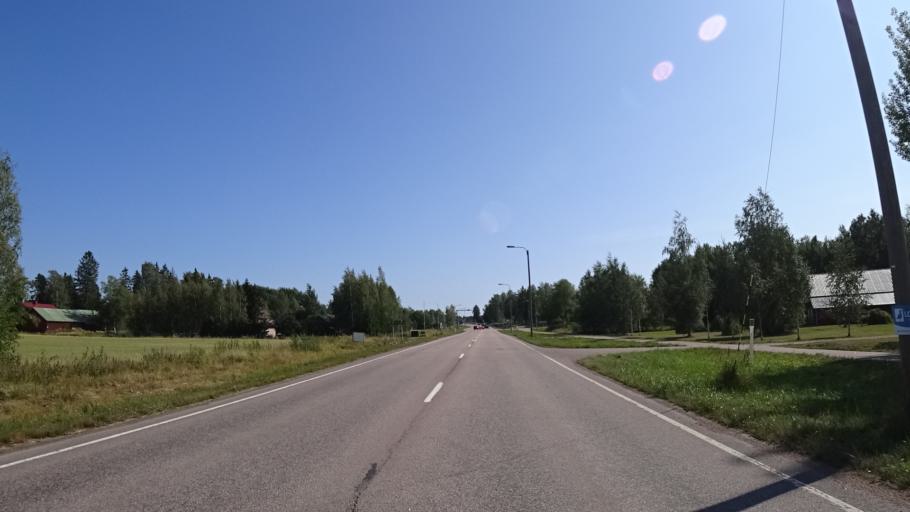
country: FI
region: Kymenlaakso
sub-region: Kotka-Hamina
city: Karhula
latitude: 60.5272
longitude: 26.9418
